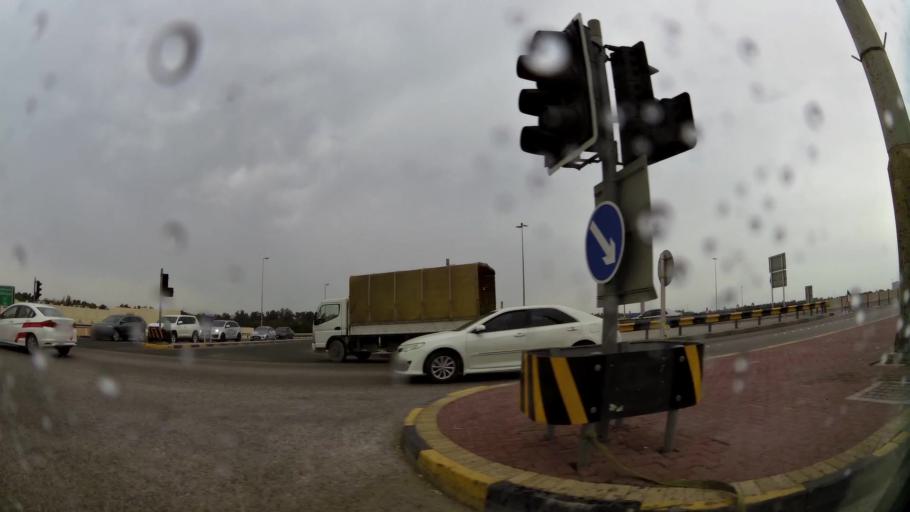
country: BH
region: Central Governorate
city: Madinat Hamad
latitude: 26.1712
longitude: 50.4655
